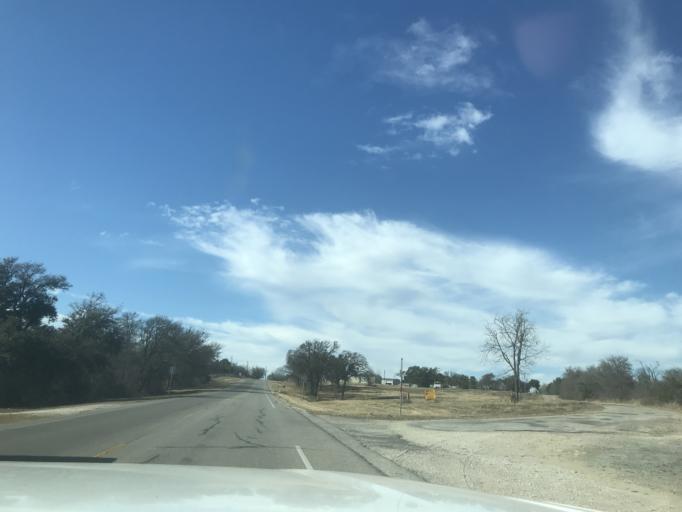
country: US
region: Texas
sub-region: Erath County
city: Stephenville
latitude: 32.2061
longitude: -98.1896
